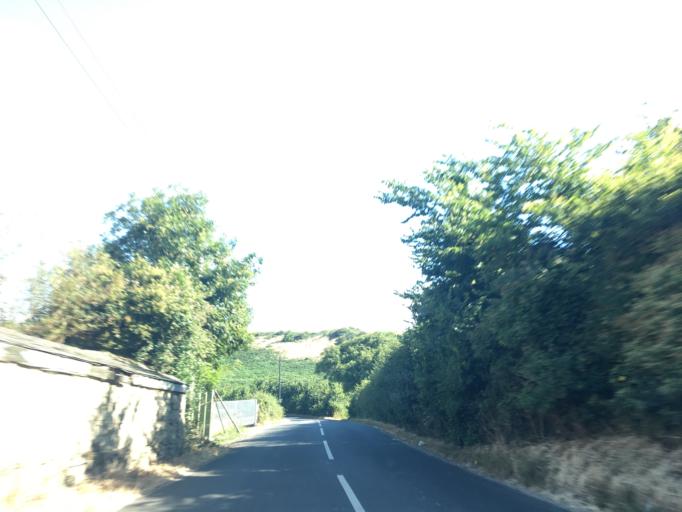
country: GB
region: England
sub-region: Isle of Wight
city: Chale
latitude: 50.6353
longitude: -1.3159
